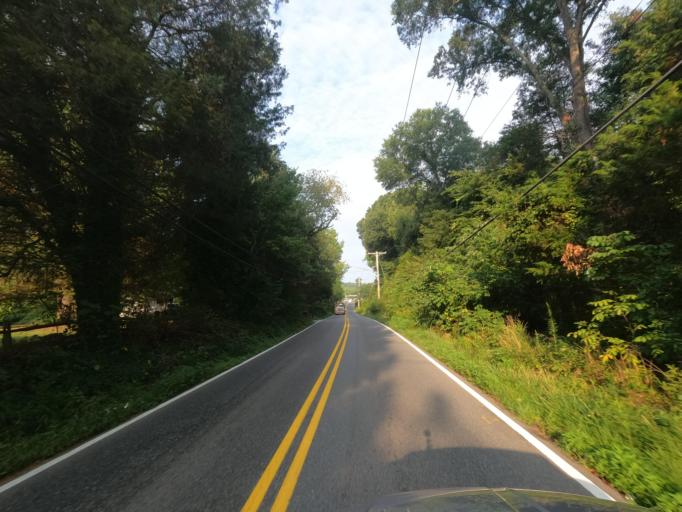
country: US
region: Maryland
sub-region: Prince George's County
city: Fort Washington
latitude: 38.6860
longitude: -76.9911
